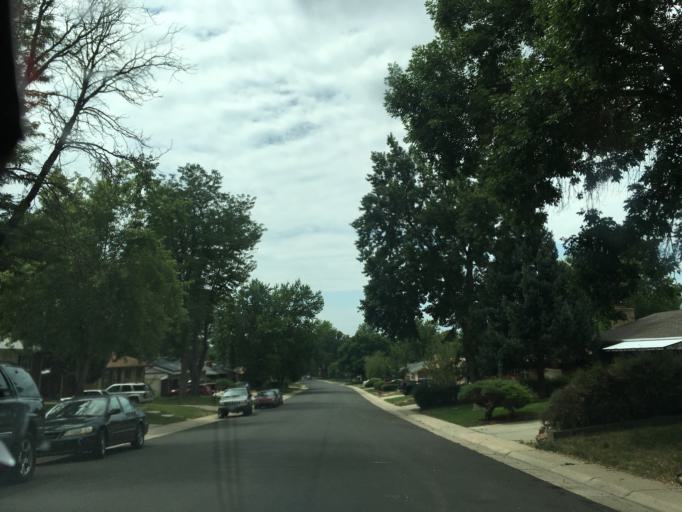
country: US
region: Colorado
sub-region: Arapahoe County
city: Sheridan
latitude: 39.6619
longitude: -105.0482
